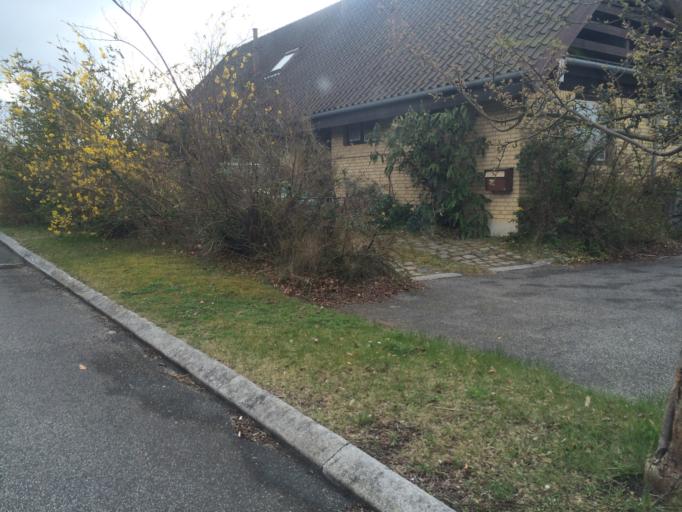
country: DK
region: Capital Region
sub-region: Ballerup Kommune
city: Ballerup
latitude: 55.7528
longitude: 12.3749
